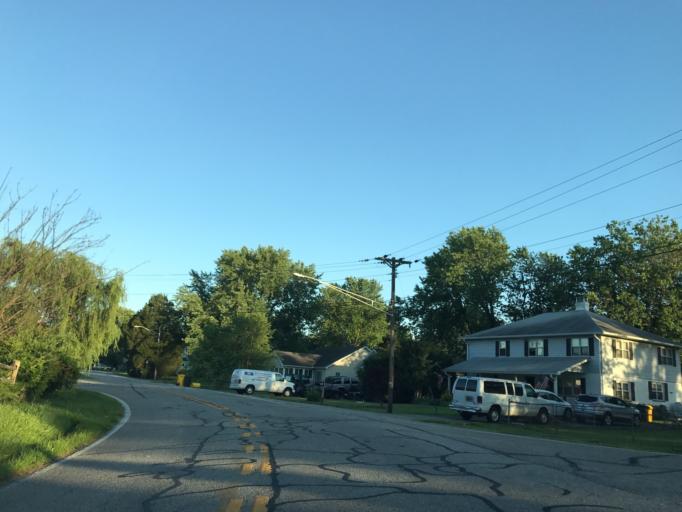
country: US
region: Maryland
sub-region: Anne Arundel County
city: Mayo
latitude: 38.8777
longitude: -76.5093
